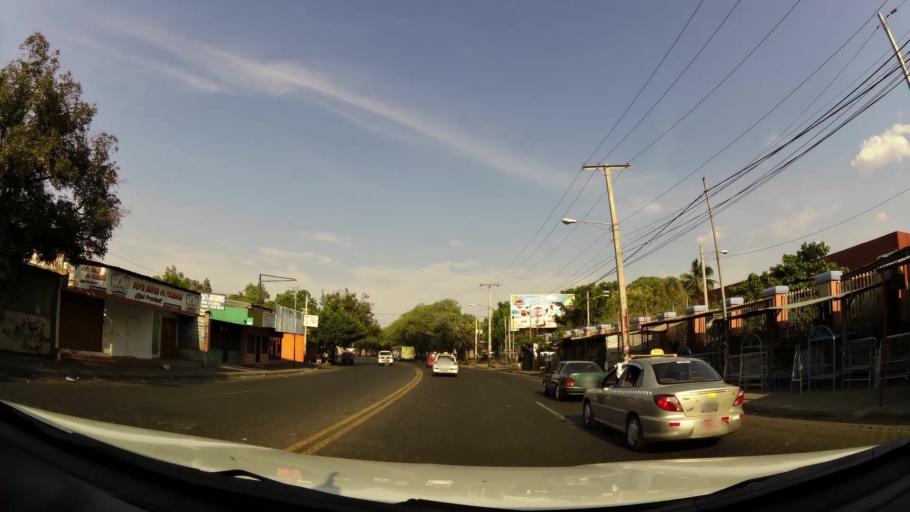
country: NI
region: Managua
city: Managua
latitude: 12.1441
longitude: -86.2633
